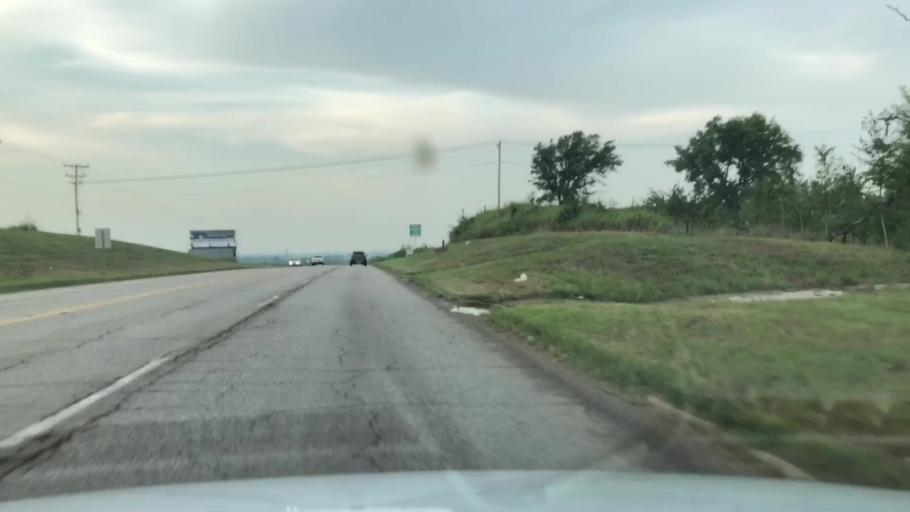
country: US
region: Oklahoma
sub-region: Washington County
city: Bartlesville
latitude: 36.6858
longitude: -95.9352
